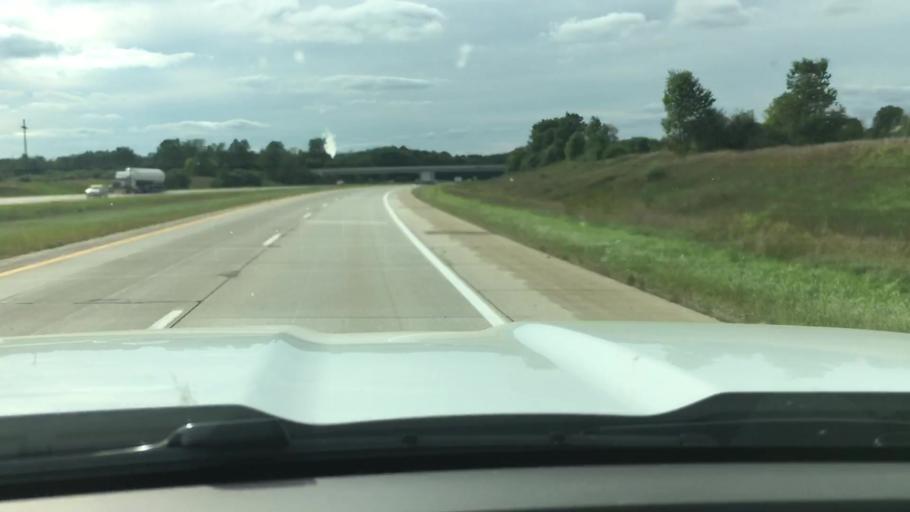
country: US
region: Michigan
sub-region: Lapeer County
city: Lapeer
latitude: 43.0121
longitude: -83.2772
